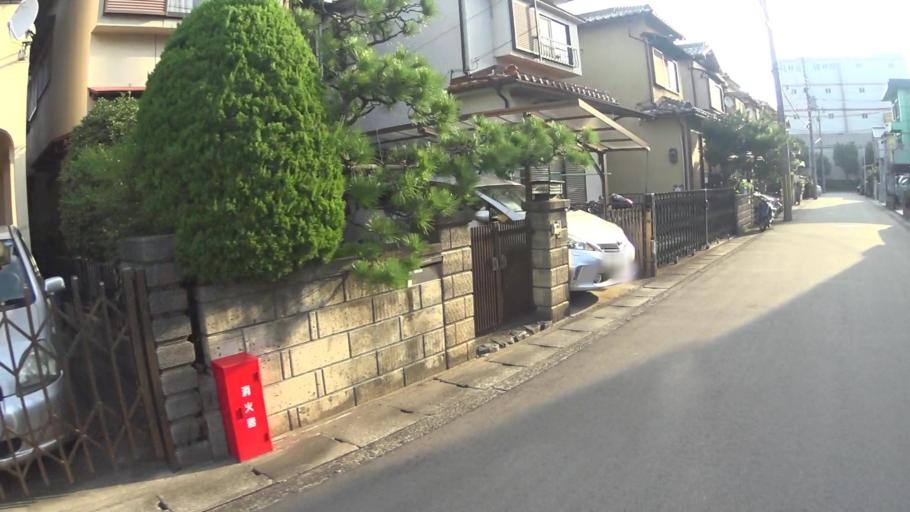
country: JP
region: Kyoto
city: Muko
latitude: 34.9332
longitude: 135.7122
